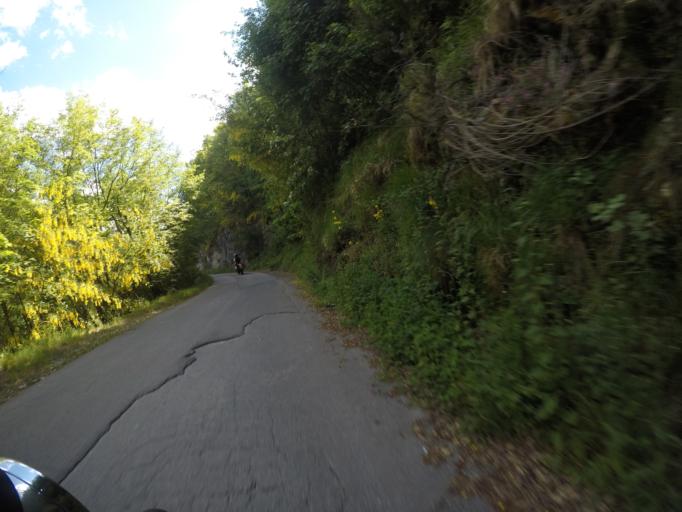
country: IT
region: Tuscany
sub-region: Provincia di Lucca
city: Minucciano
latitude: 44.1530
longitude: 10.1994
